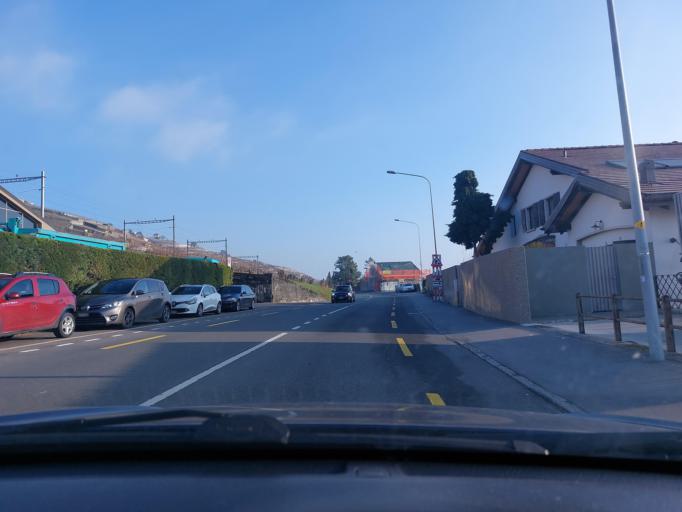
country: CH
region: Vaud
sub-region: Lavaux-Oron District
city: Lutry
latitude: 46.4983
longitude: 6.7012
